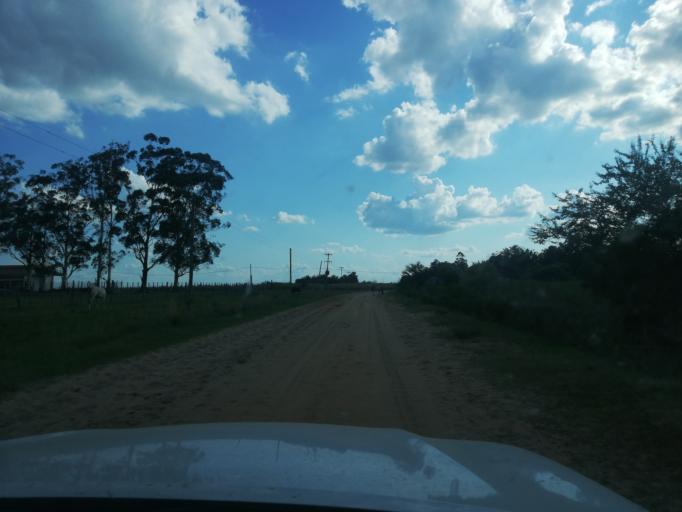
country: AR
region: Corrientes
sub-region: Departamento de San Miguel
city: San Miguel
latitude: -27.9969
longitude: -57.5797
